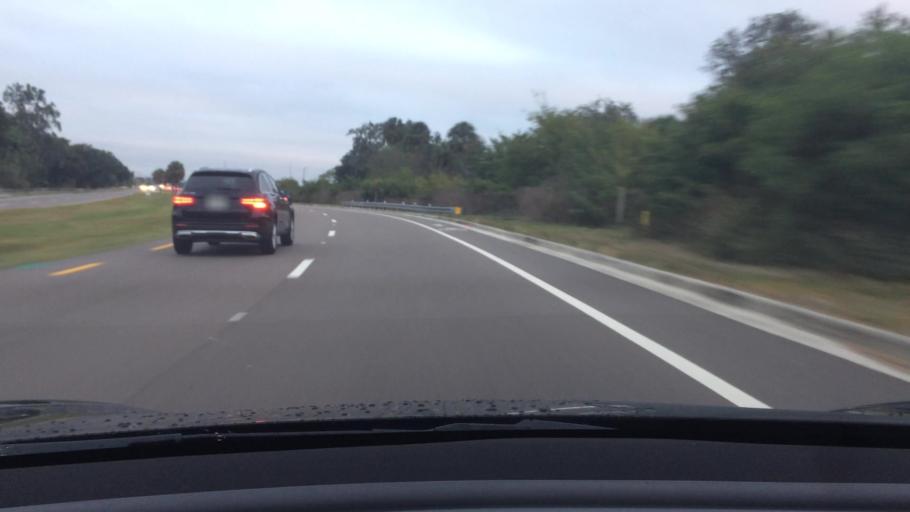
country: US
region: Florida
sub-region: Hillsborough County
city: Progress Village
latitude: 27.8938
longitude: -82.3565
